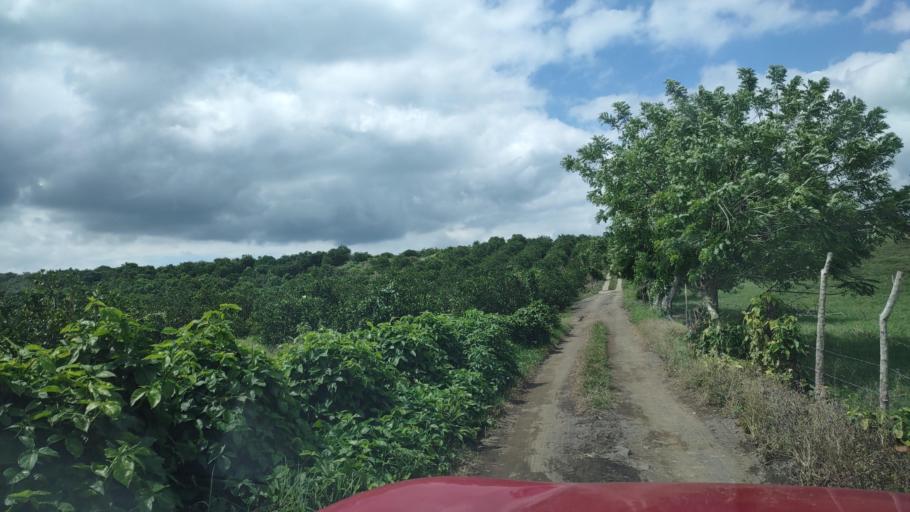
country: MX
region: Puebla
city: San Jose Acateno
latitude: 20.2191
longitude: -97.1397
